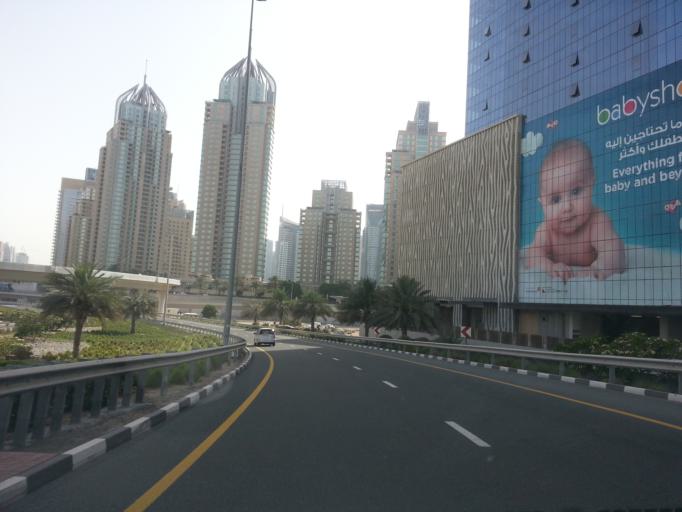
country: AE
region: Dubai
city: Dubai
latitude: 25.0873
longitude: 55.1521
